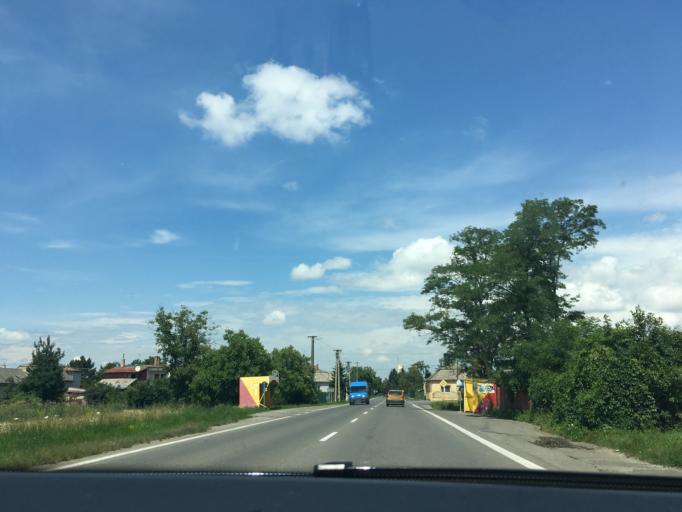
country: SK
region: Kosicky
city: Trebisov
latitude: 48.6720
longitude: 21.7127
